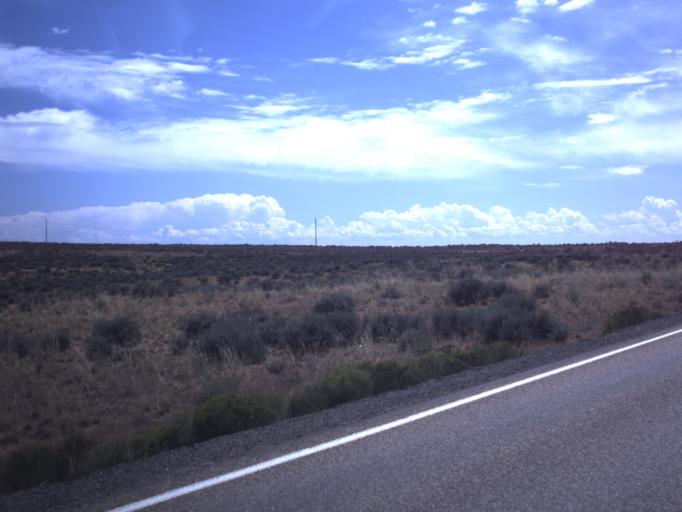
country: US
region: Utah
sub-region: Uintah County
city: Maeser
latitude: 40.2928
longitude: -109.6859
